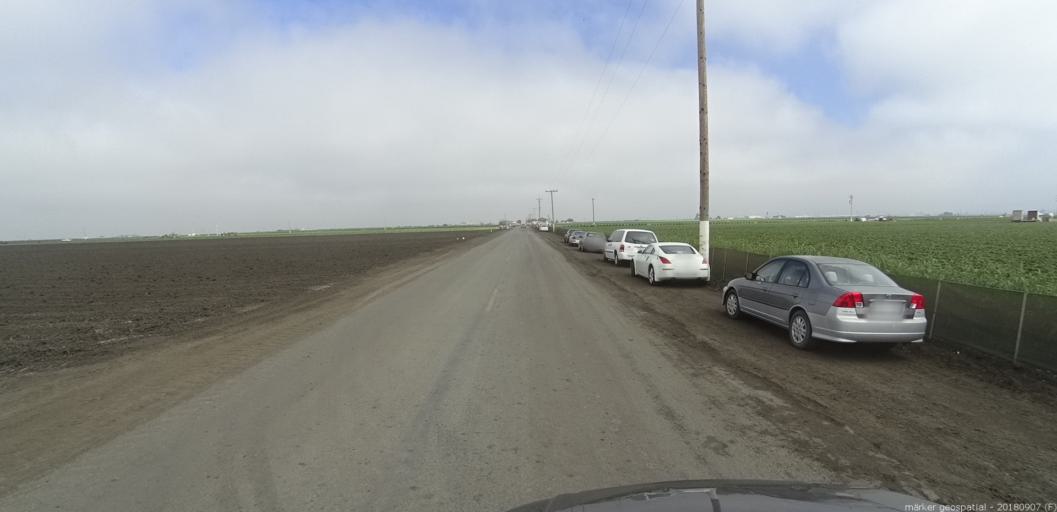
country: US
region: California
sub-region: Monterey County
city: Boronda
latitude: 36.6818
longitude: -121.7079
